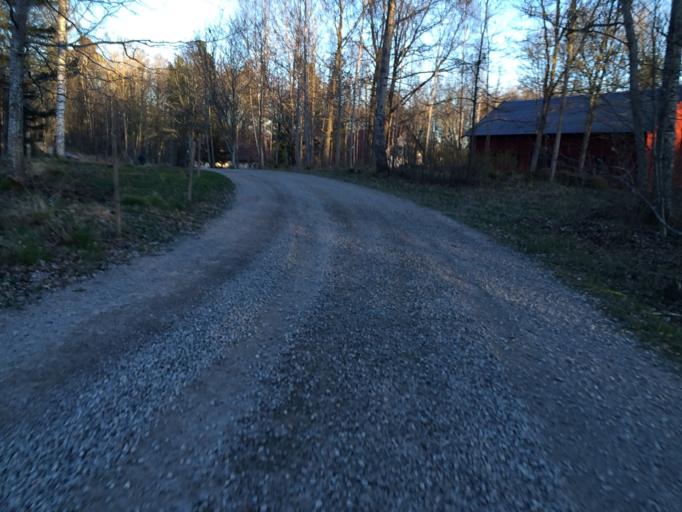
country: SE
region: Soedermanland
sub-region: Eskilstuna Kommun
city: Kvicksund
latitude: 59.4505
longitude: 16.3446
